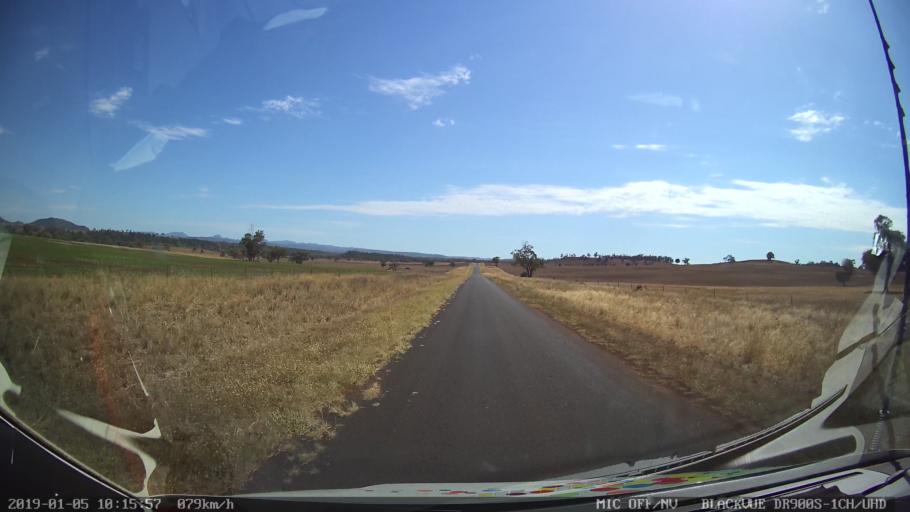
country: AU
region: New South Wales
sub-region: Gilgandra
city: Gilgandra
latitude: -31.5798
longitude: 148.9478
